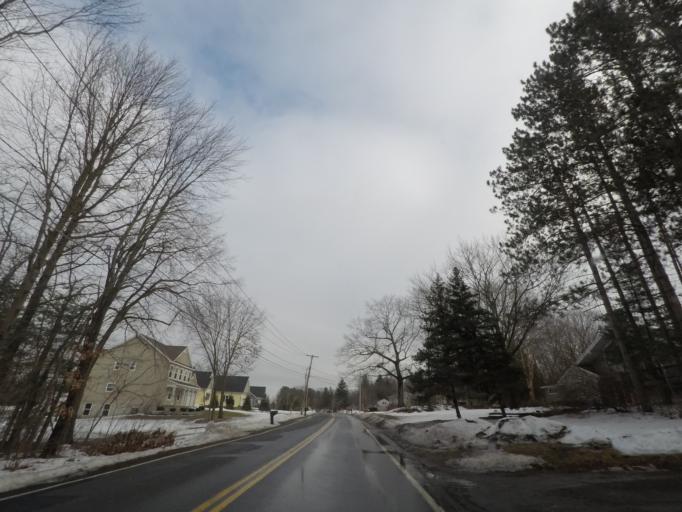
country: US
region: New York
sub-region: Schenectady County
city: Rotterdam
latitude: 42.7255
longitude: -73.9429
